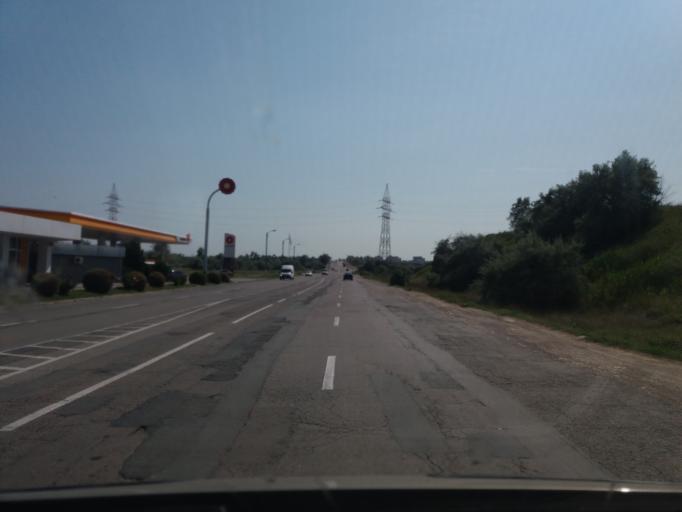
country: RO
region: Constanta
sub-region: Comuna Navodari
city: Navodari
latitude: 44.3284
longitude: 28.6274
